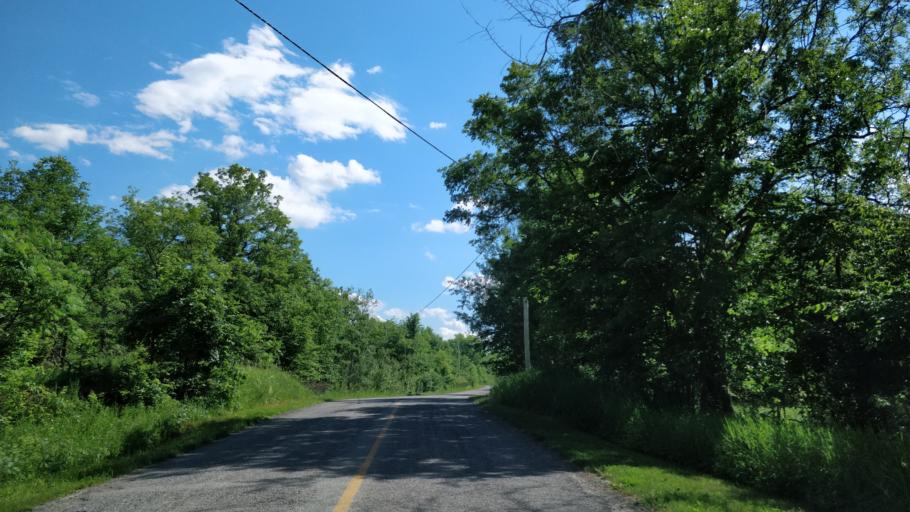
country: CA
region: Ontario
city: Perth
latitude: 44.7367
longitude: -76.5027
